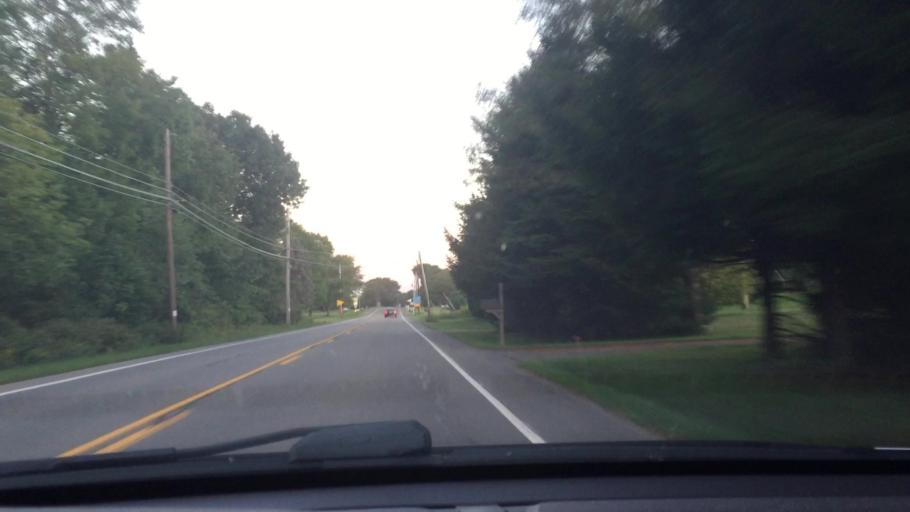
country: US
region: Pennsylvania
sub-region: Butler County
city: Slippery Rock
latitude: 41.1152
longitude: -80.0575
